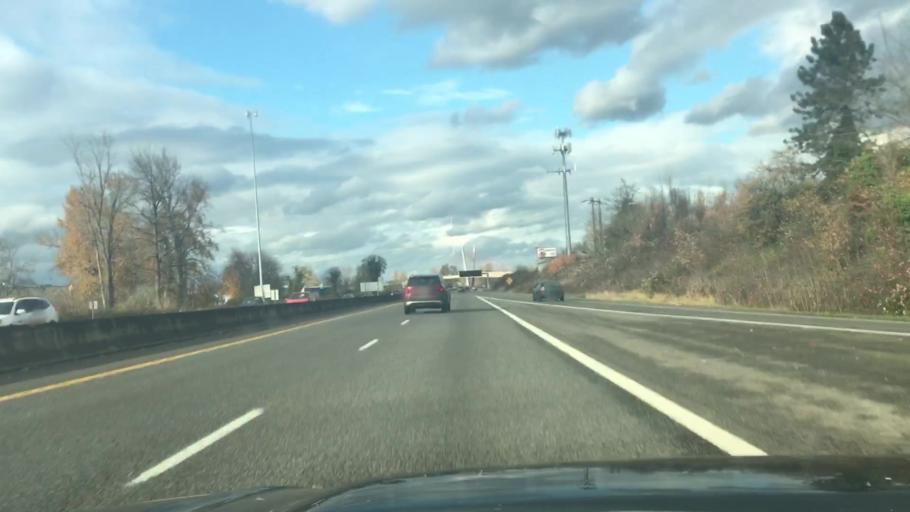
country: US
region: Oregon
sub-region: Lane County
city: Eugene
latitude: 44.0718
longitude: -123.1027
